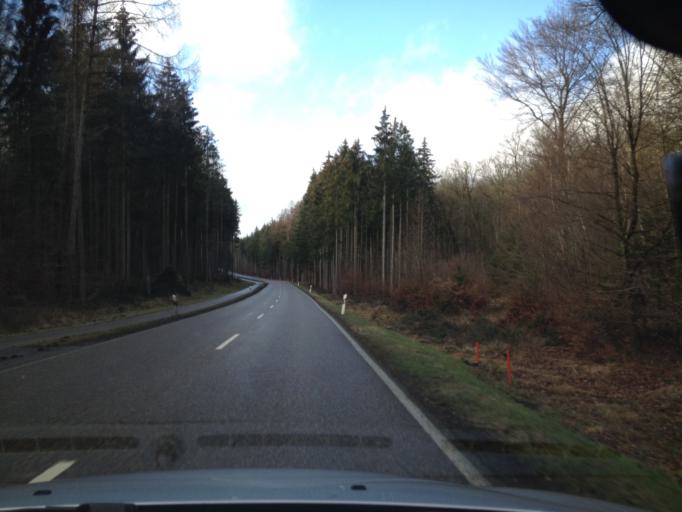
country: DE
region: Bavaria
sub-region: Swabia
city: Grossaitingen
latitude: 48.2601
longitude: 10.7628
